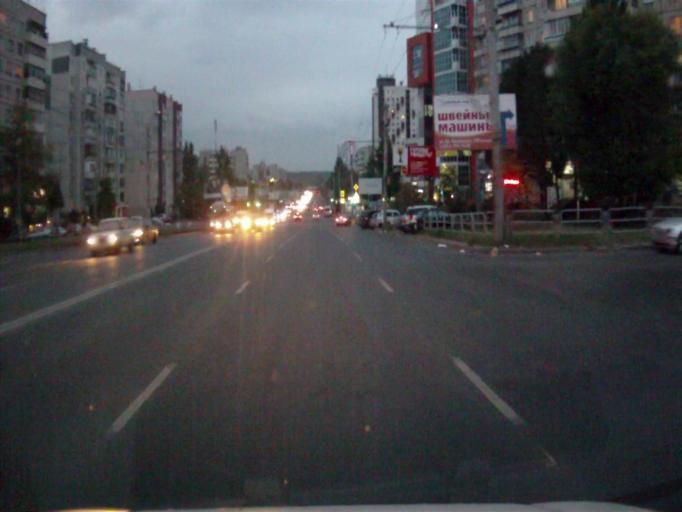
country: RU
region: Chelyabinsk
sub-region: Gorod Chelyabinsk
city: Chelyabinsk
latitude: 55.1853
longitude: 61.3325
